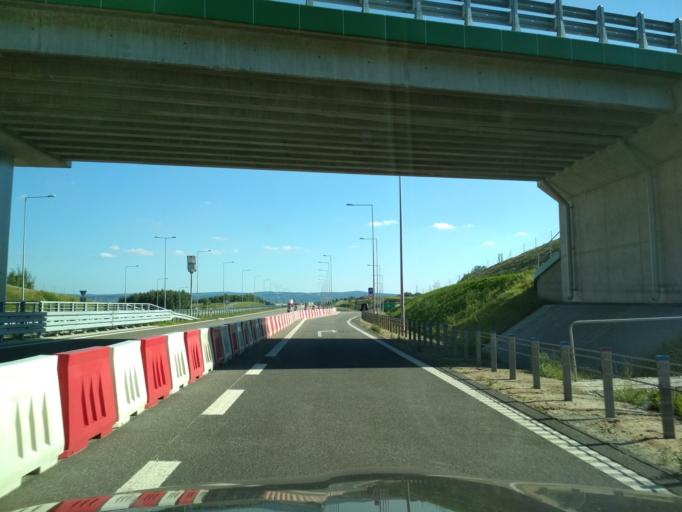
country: PL
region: Subcarpathian Voivodeship
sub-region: Powiat rzeszowski
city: Kielanowka
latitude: 50.0174
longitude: 21.9215
